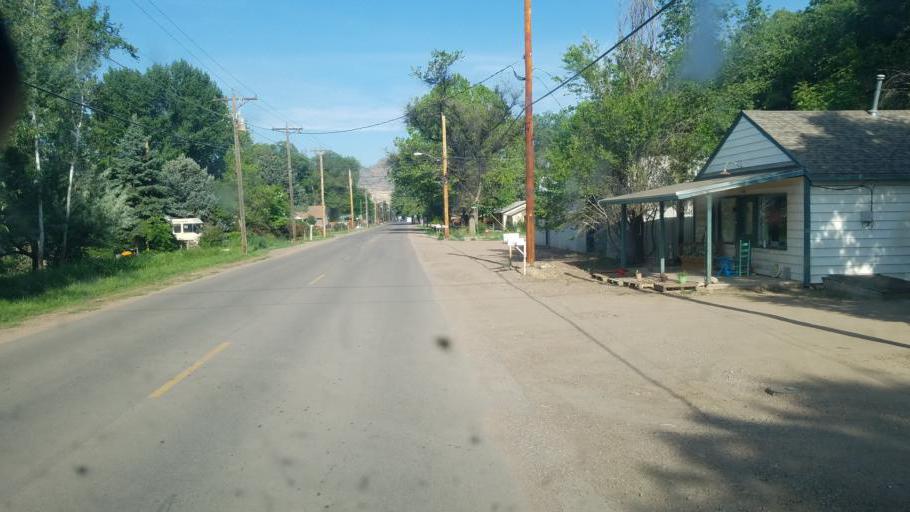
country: US
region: Colorado
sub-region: Fremont County
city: Lincoln Park
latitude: 38.4467
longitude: -105.2151
